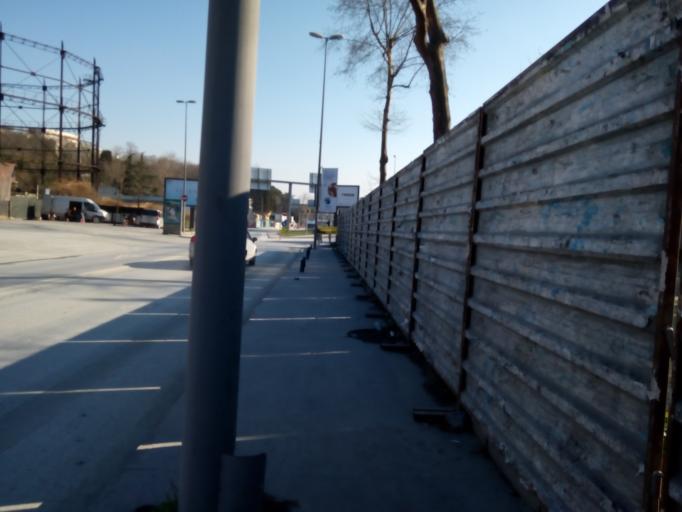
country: TR
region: Istanbul
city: Sisli
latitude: 41.0427
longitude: 28.9928
